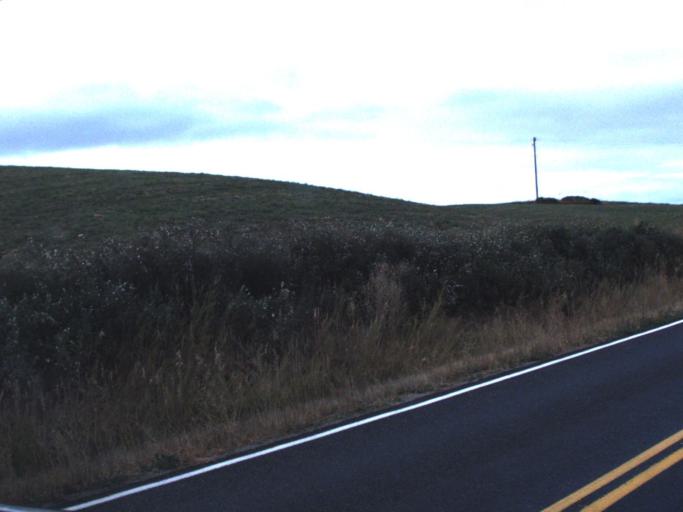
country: US
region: Washington
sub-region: Stevens County
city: Chewelah
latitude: 48.1185
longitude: -117.7540
